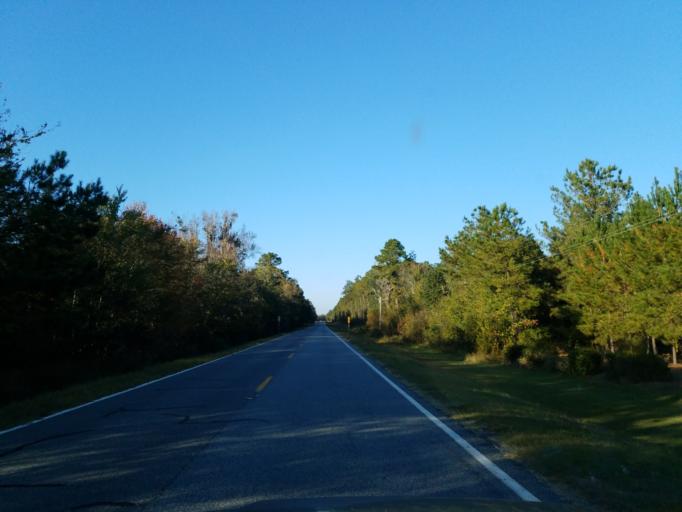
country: US
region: Georgia
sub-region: Lanier County
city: Lakeland
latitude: 30.9579
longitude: -83.0819
